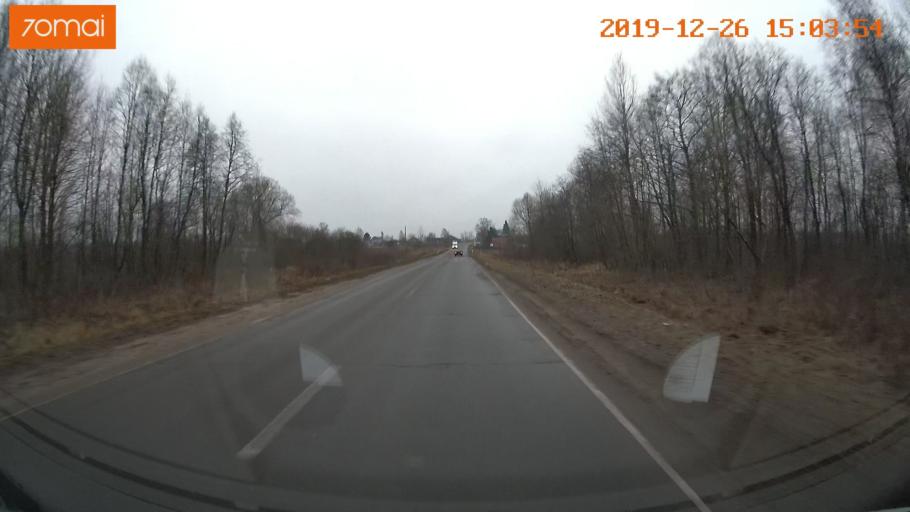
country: RU
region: Jaroslavl
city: Rybinsk
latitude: 58.2062
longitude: 38.8670
